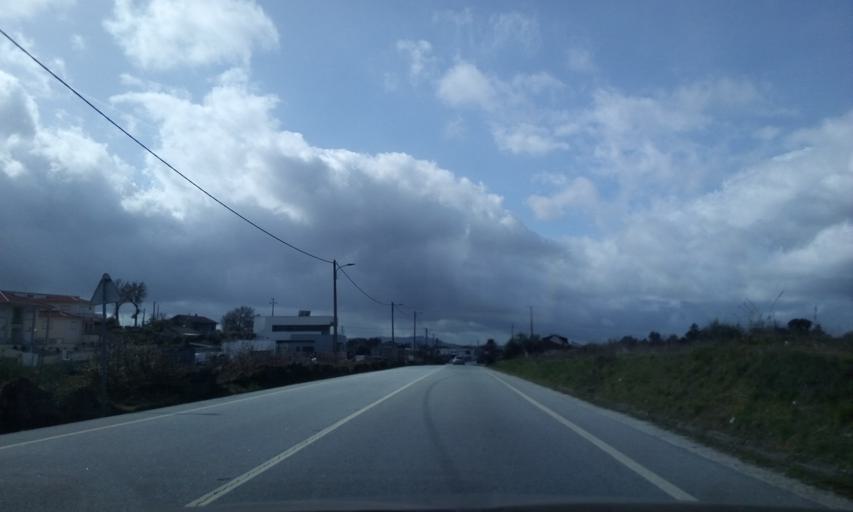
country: PT
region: Viseu
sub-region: Satao
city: Satao
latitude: 40.6689
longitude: -7.7112
